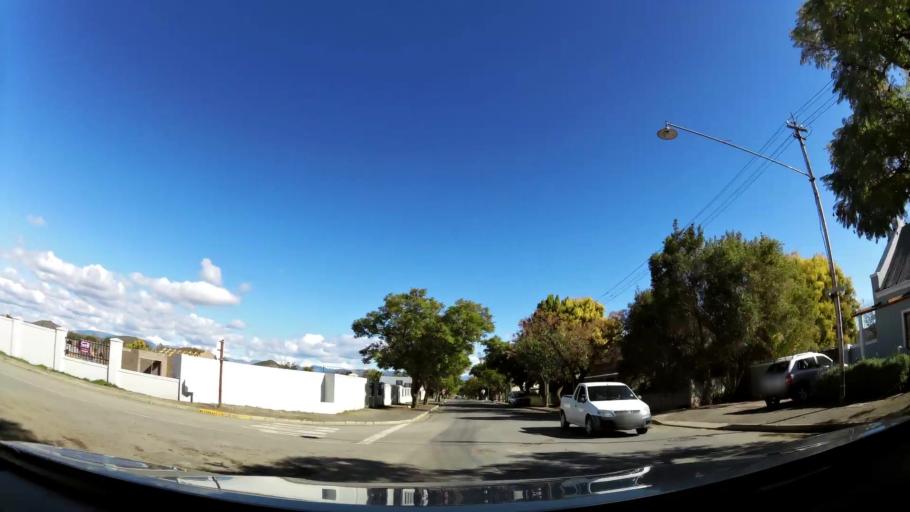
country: ZA
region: Western Cape
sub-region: Cape Winelands District Municipality
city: Ashton
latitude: -33.7974
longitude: 19.8897
